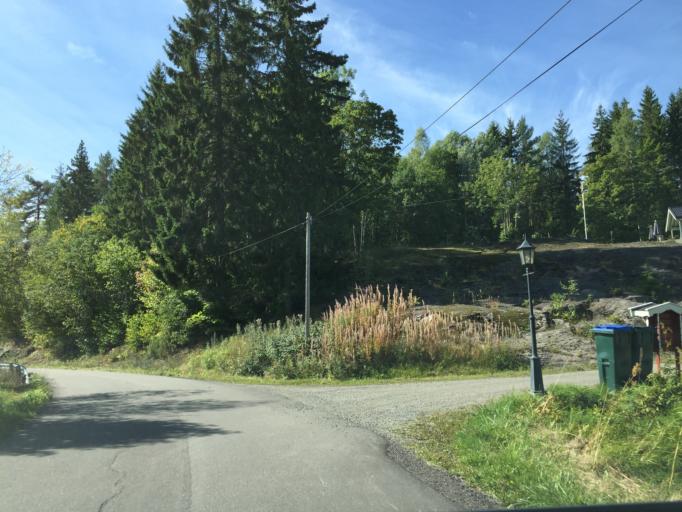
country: NO
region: Vestfold
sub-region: Hof
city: Hof
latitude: 59.4746
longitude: 10.1437
